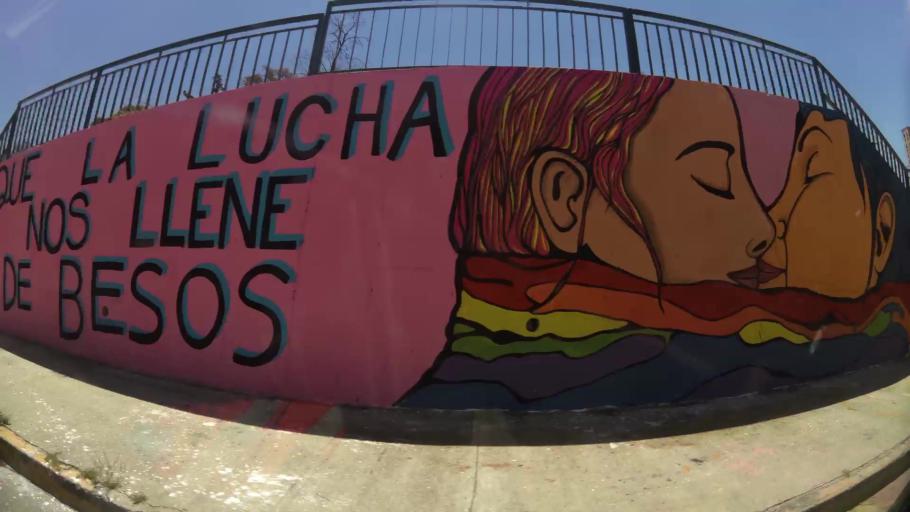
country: AR
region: Cordoba
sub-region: Departamento de Capital
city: Cordoba
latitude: -31.4059
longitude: -64.1834
